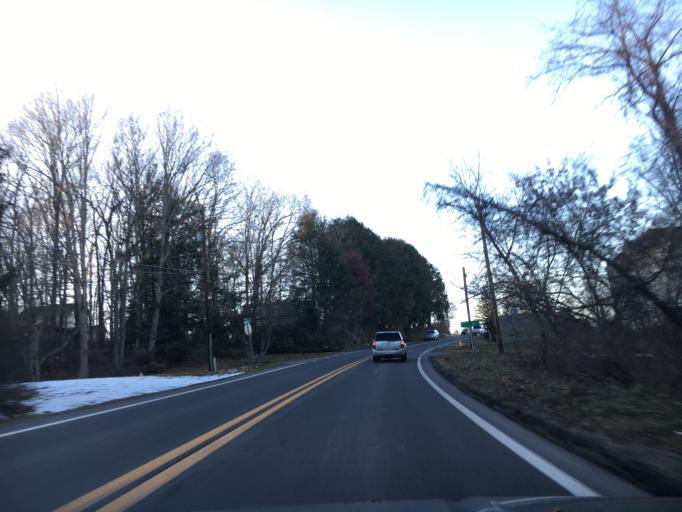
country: US
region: West Virginia
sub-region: Raleigh County
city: Beaver
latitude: 37.7673
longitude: -81.1585
